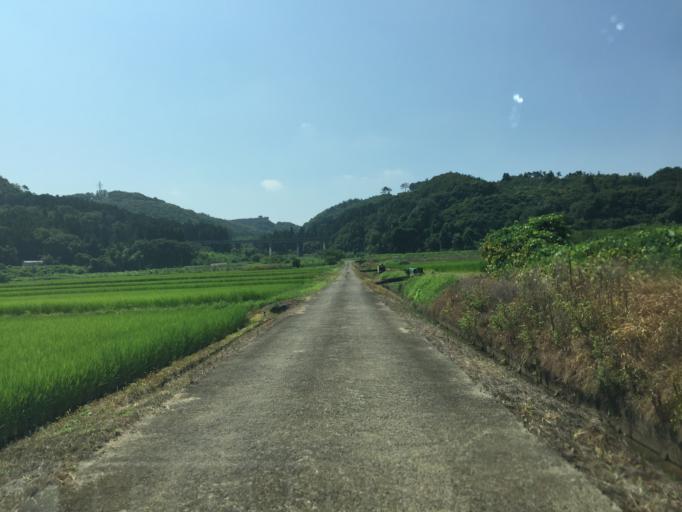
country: JP
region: Fukushima
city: Fukushima-shi
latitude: 37.7066
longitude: 140.4550
